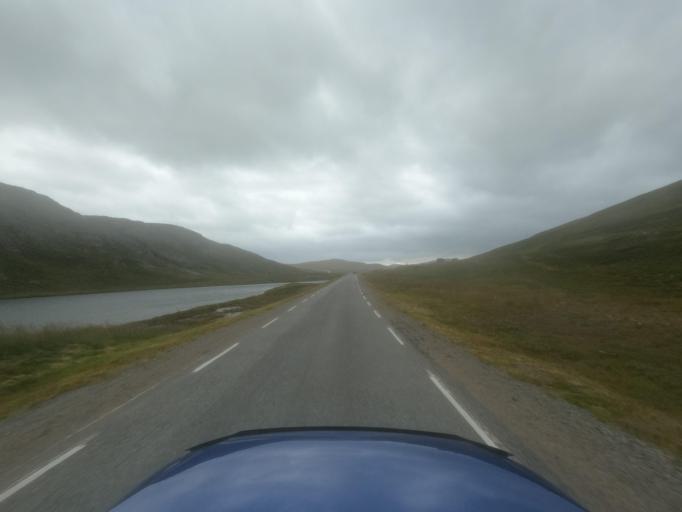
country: NO
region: Finnmark Fylke
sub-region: Nordkapp
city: Honningsvag
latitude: 71.0955
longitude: 25.7908
